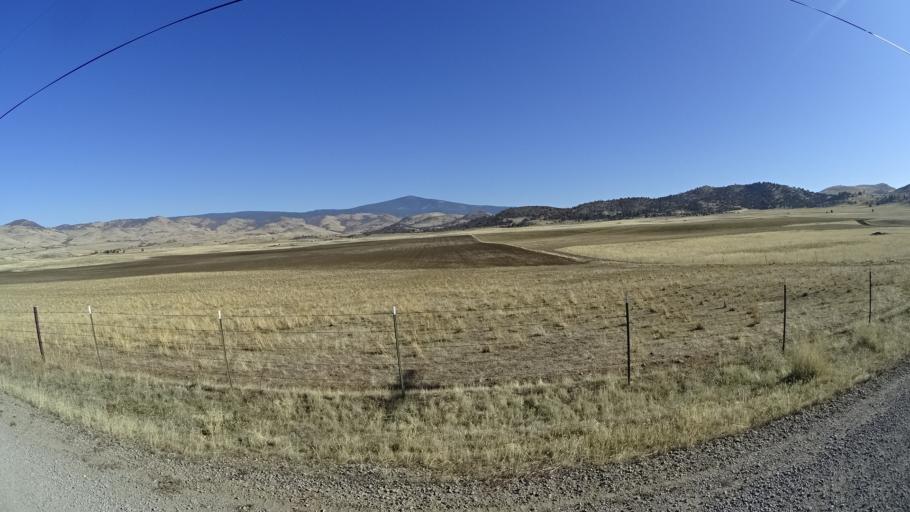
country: US
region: California
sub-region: Siskiyou County
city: Montague
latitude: 41.8008
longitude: -122.4159
